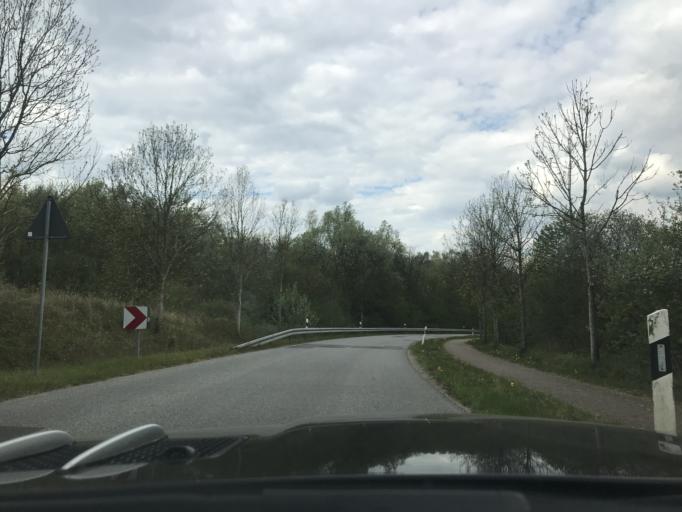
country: DE
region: Schleswig-Holstein
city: Gross Gronau
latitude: 53.7724
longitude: 10.7699
